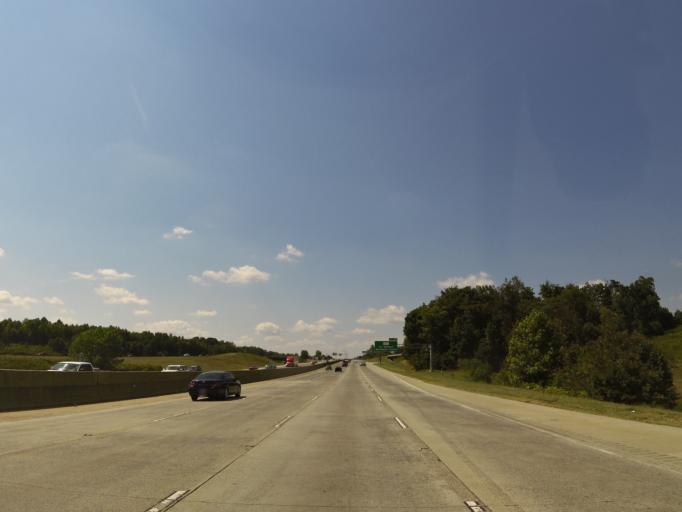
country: US
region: North Carolina
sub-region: Gaston County
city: Mount Holly
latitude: 35.2500
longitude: -80.9707
